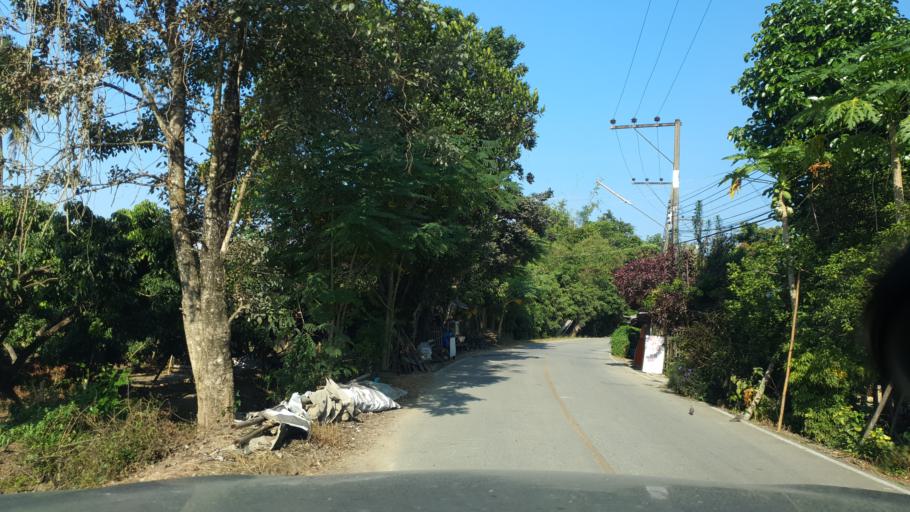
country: TH
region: Chiang Mai
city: Saraphi
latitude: 18.6993
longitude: 99.0776
